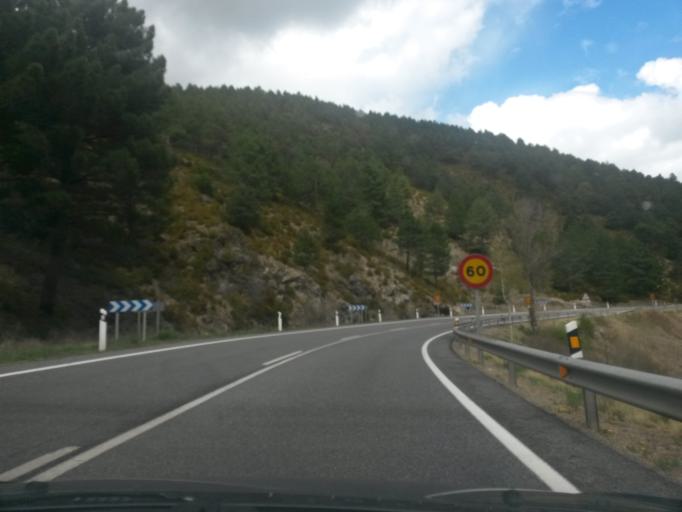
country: ES
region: Catalonia
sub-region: Provincia de Lleida
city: Lles de Cerdanya
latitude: 42.3637
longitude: 1.7053
